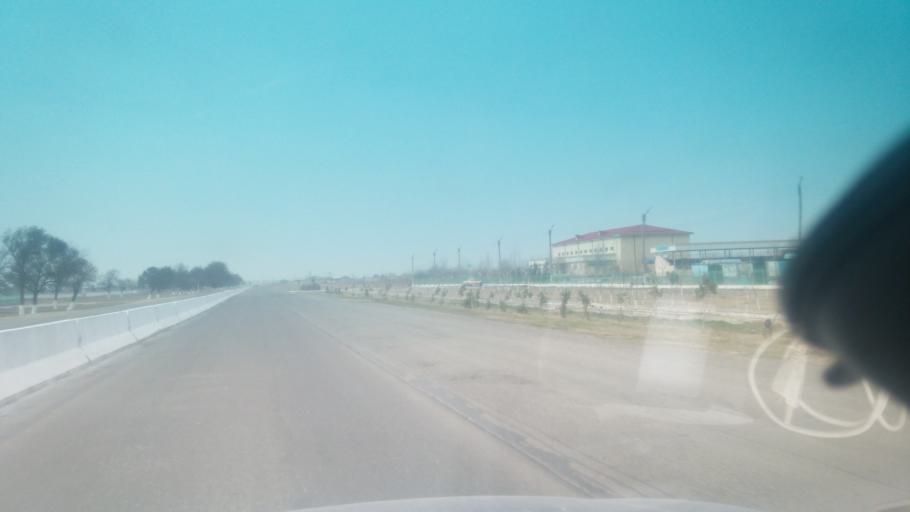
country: UZ
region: Sirdaryo
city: Yangiyer
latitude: 40.2276
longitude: 68.8347
